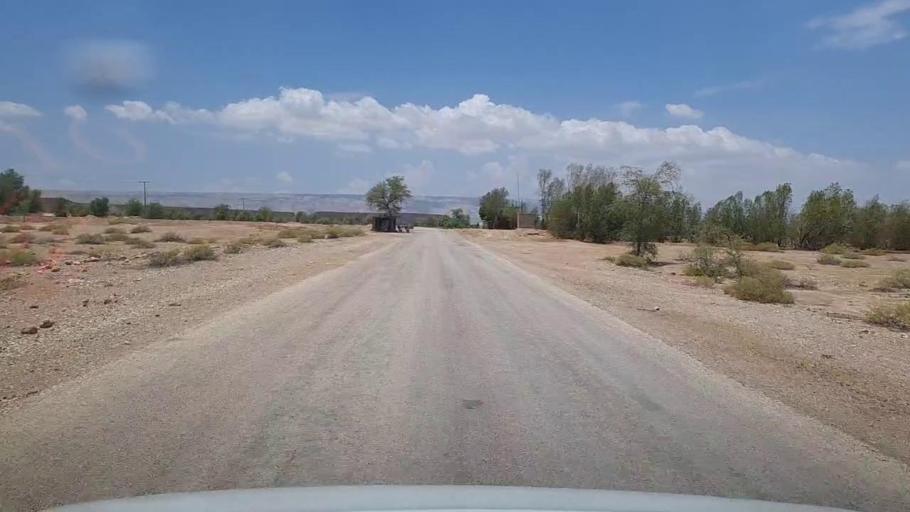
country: PK
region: Sindh
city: Bhan
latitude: 26.3175
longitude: 67.6015
